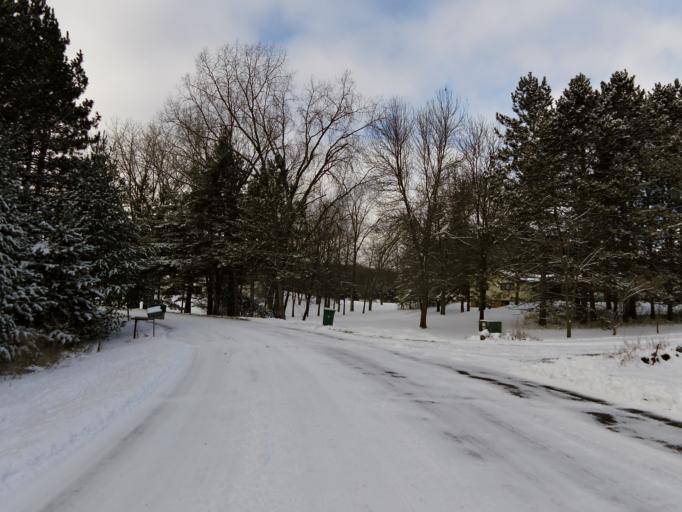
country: US
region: Minnesota
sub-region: Washington County
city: Lake Elmo
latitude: 44.9767
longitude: -92.8333
